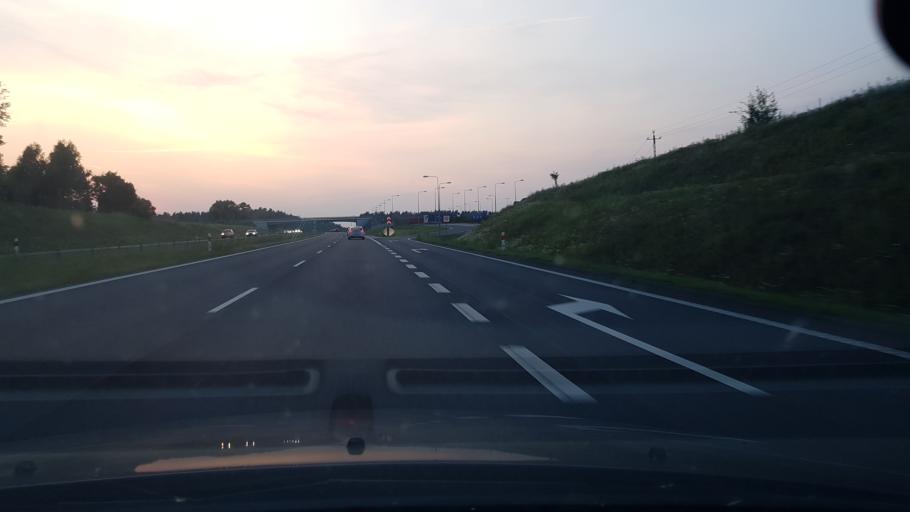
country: PL
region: Warmian-Masurian Voivodeship
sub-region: Powiat olsztynski
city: Olsztynek
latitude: 53.5128
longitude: 20.3008
